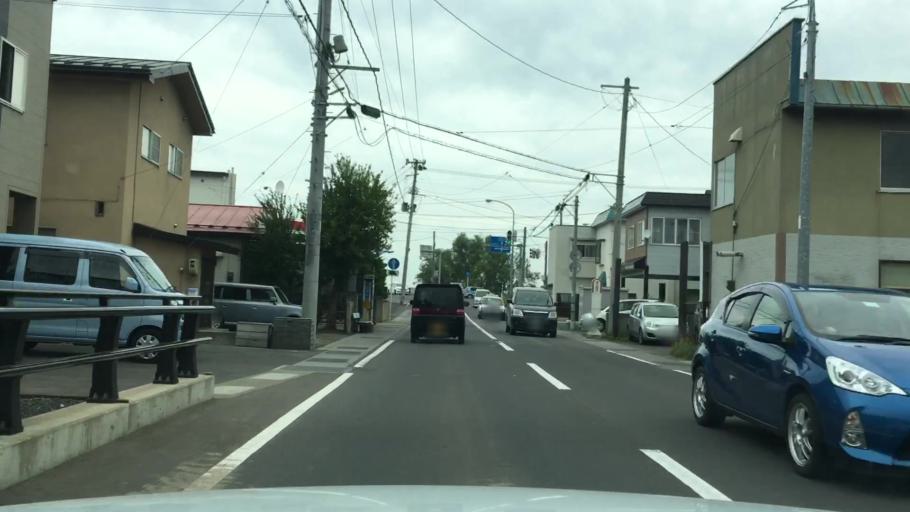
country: JP
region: Aomori
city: Hirosaki
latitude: 40.6140
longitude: 140.4620
